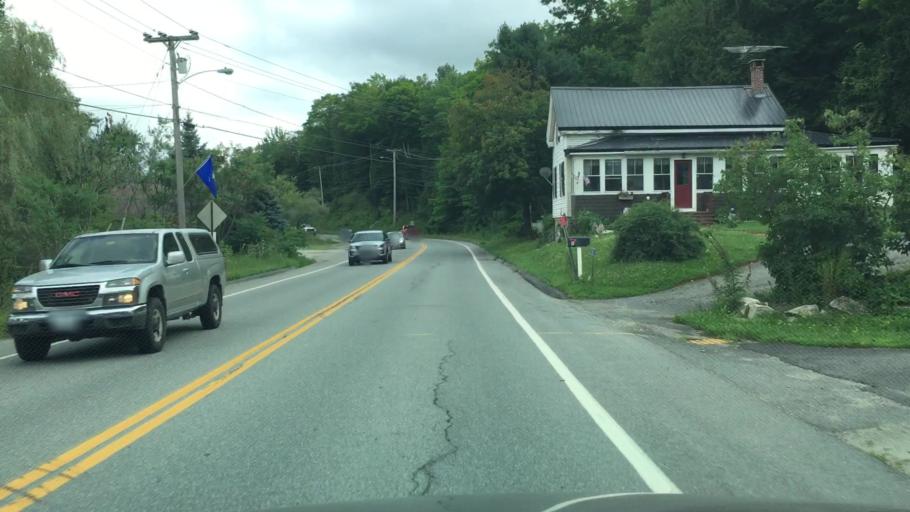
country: US
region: Maine
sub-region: Waldo County
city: Frankfort
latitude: 44.6073
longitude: -68.8738
